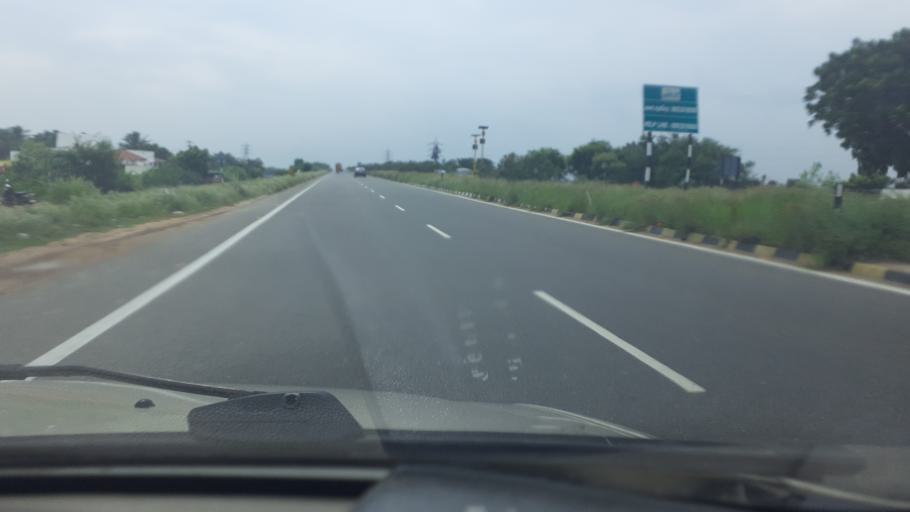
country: IN
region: Tamil Nadu
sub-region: Madurai
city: Tirupparangunram
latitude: 9.8370
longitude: 77.9853
